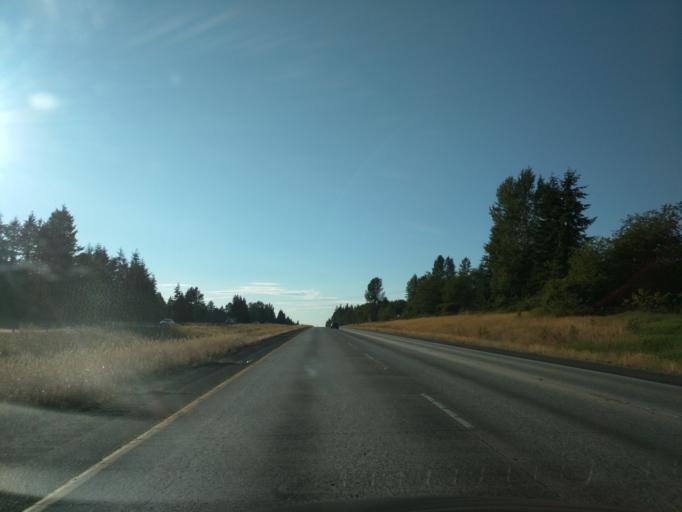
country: US
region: Washington
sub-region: Snohomish County
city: Stanwood
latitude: 48.2885
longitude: -122.2929
